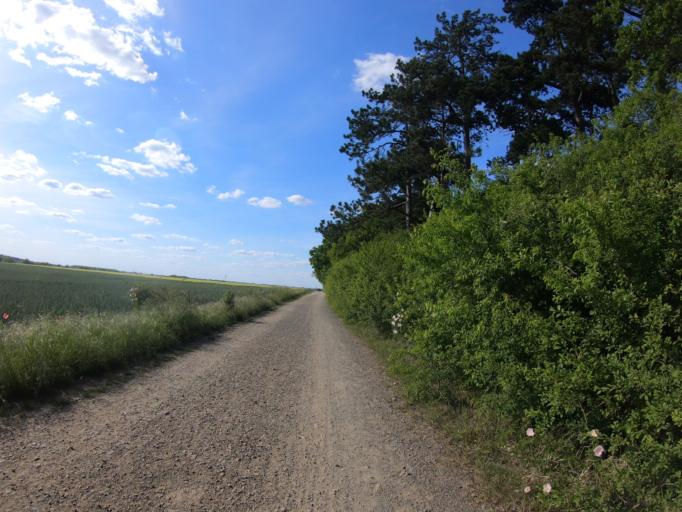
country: DE
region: Lower Saxony
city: Leiferde
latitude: 52.1900
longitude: 10.5274
